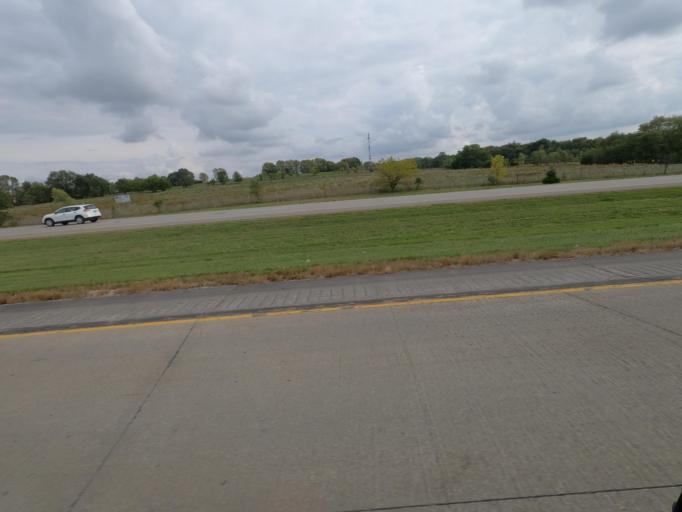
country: US
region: Iowa
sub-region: Polk County
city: Altoona
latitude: 41.6160
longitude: -93.4940
